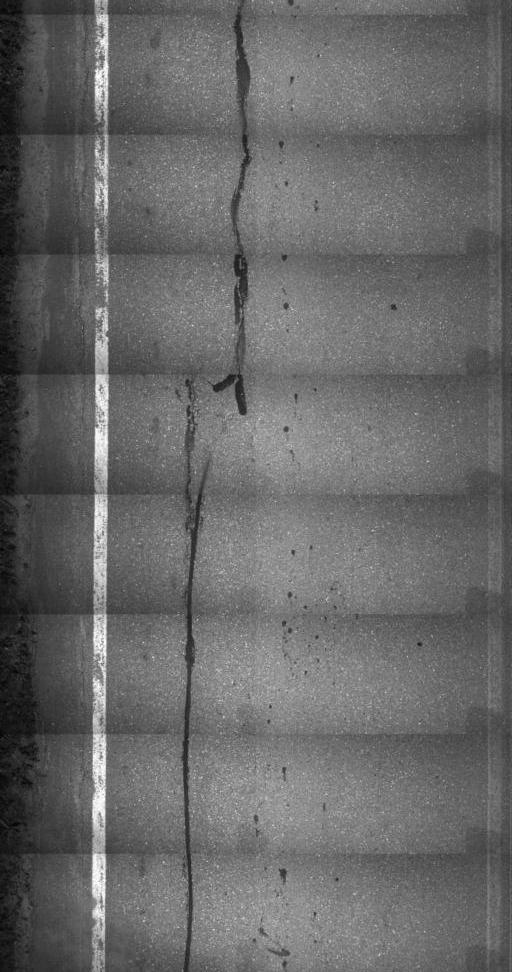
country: US
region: Vermont
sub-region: Orleans County
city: Newport
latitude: 44.9928
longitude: -72.3876
